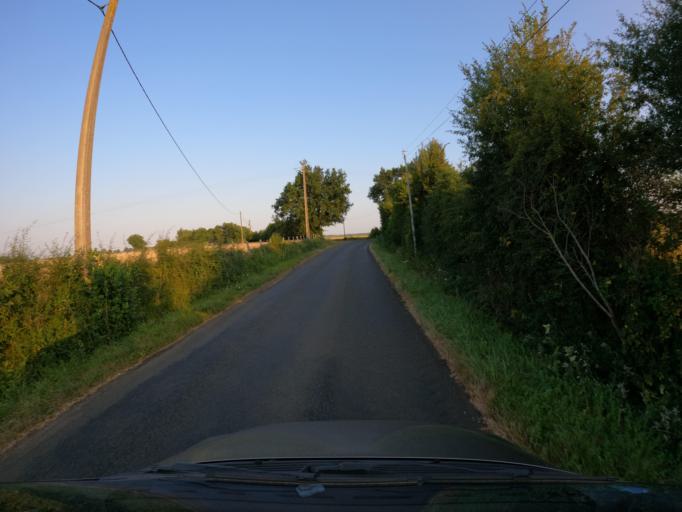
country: FR
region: Pays de la Loire
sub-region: Departement de la Sarthe
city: Parce-sur-Sarthe
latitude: 47.8986
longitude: -0.2190
